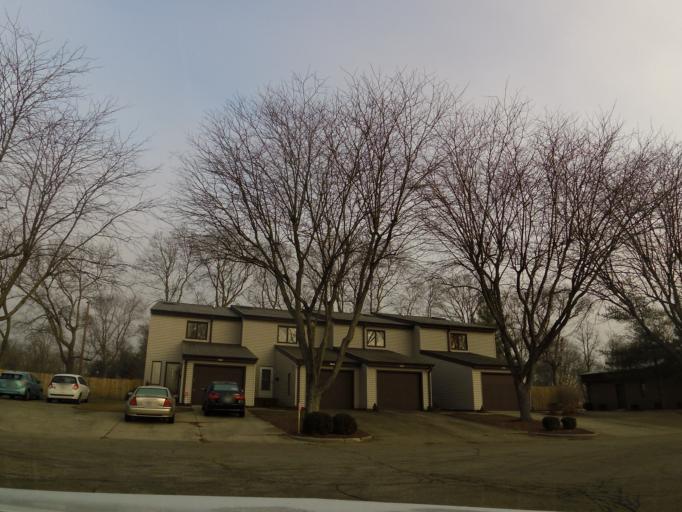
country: US
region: Indiana
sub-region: Bartholomew County
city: Columbus
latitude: 39.2297
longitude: -85.9086
